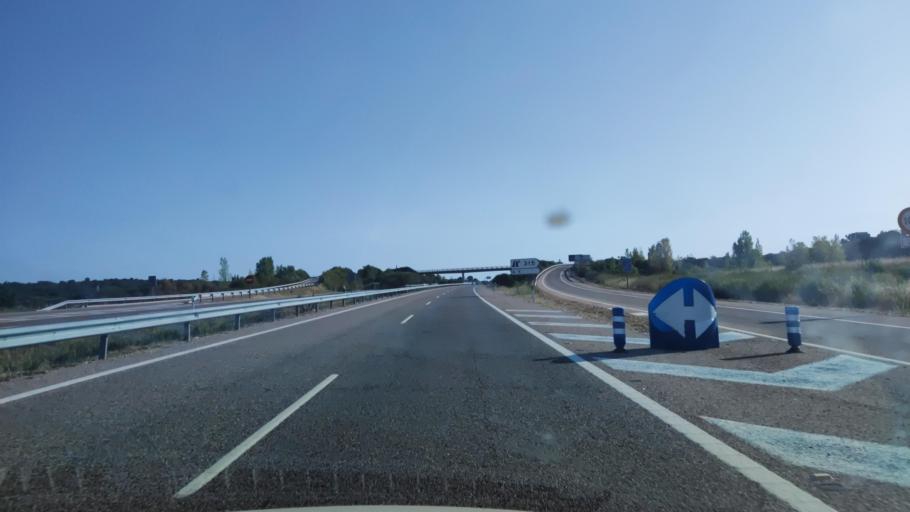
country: ES
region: Castille and Leon
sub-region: Provincia de Salamanca
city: Tenebron
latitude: 40.6692
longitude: -6.4323
